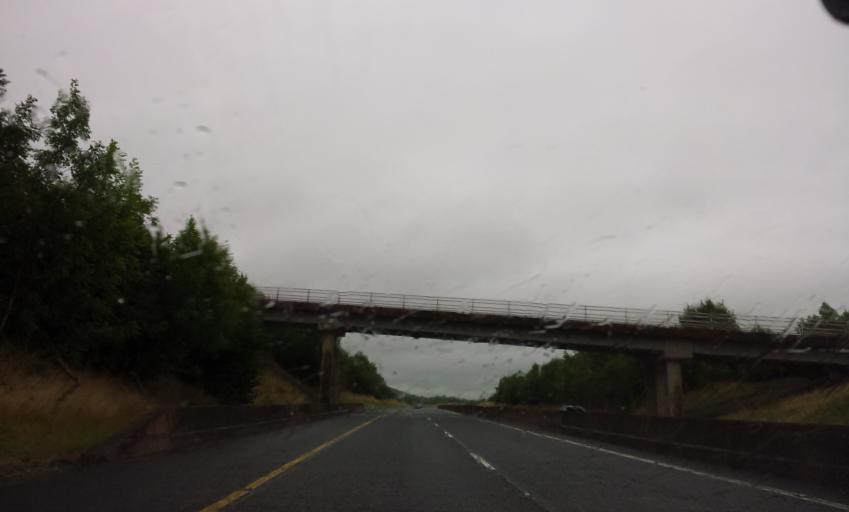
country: IE
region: Munster
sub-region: County Cork
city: Rathcormac
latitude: 52.0872
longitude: -8.2938
